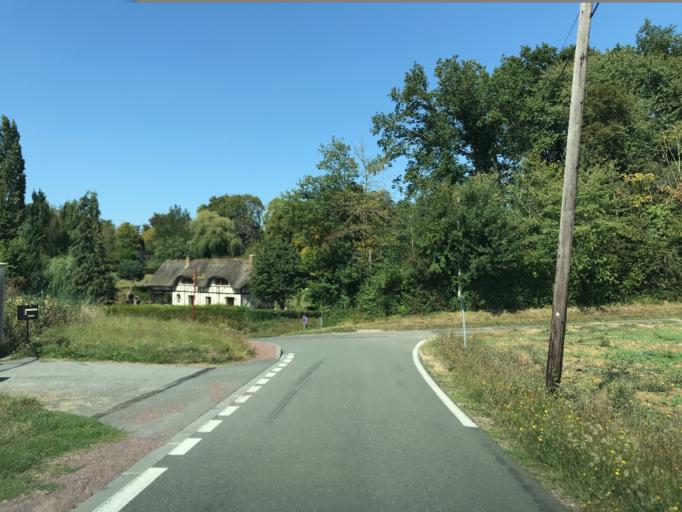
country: FR
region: Haute-Normandie
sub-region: Departement de l'Eure
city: Gravigny
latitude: 49.0760
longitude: 1.2569
